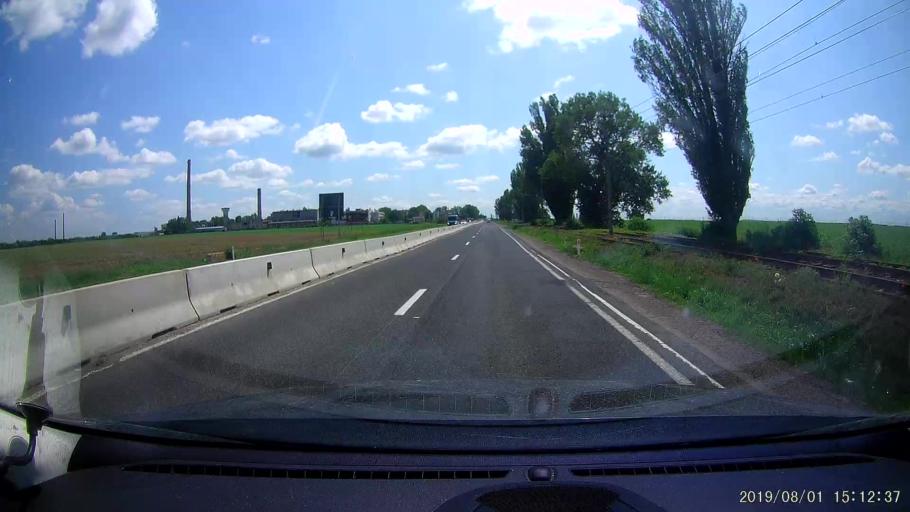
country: RO
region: Braila
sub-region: Comuna Chiscani
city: Lacu Sarat
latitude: 45.2042
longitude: 27.9113
